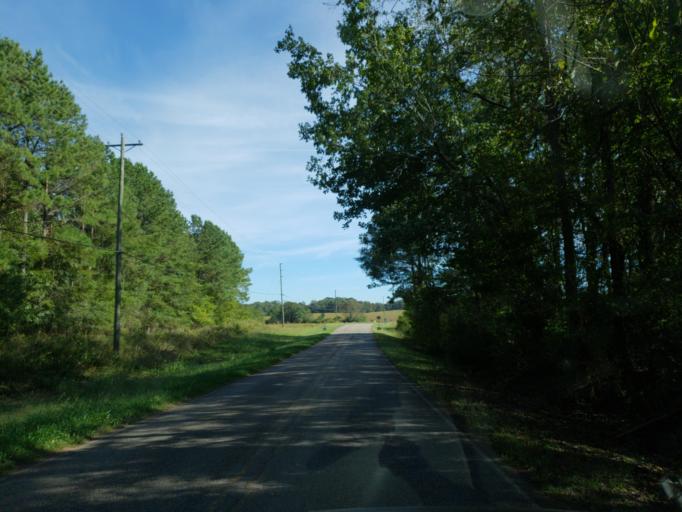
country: US
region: Georgia
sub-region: Crawford County
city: Roberta
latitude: 32.8501
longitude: -84.0797
